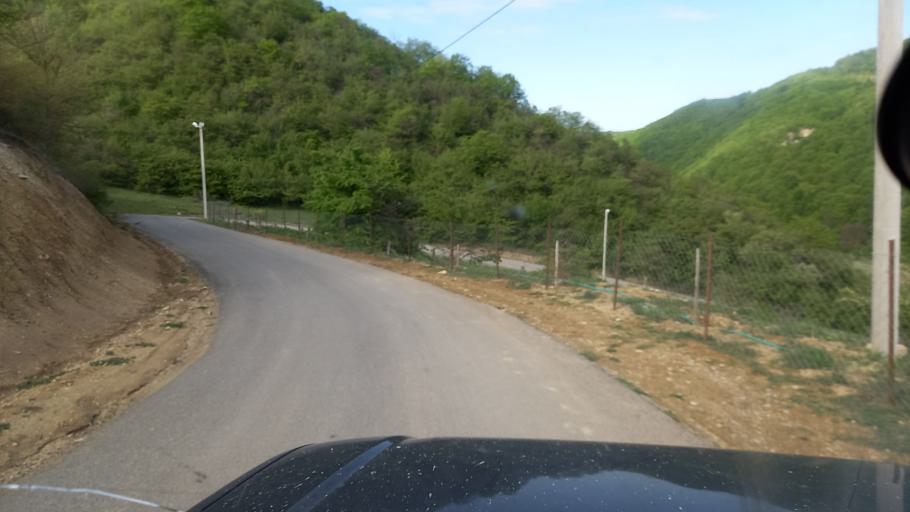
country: RU
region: Dagestan
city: Khuchni
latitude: 41.9661
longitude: 47.9574
